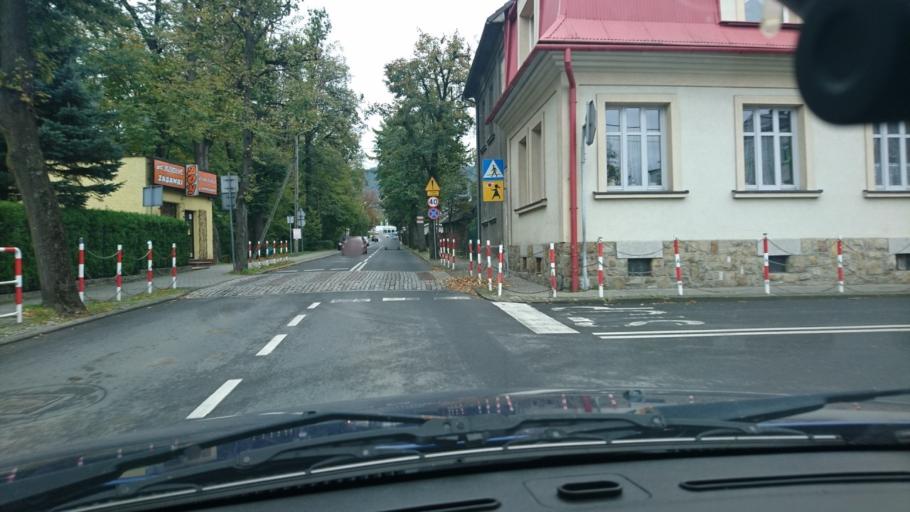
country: PL
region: Silesian Voivodeship
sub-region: Powiat bielski
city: Kozy
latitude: 49.8462
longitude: 19.1404
